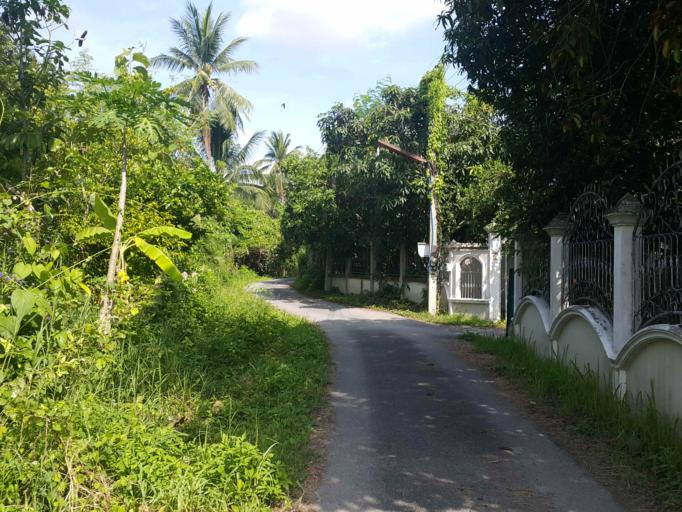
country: TH
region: Chiang Mai
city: San Sai
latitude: 18.8059
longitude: 99.0923
